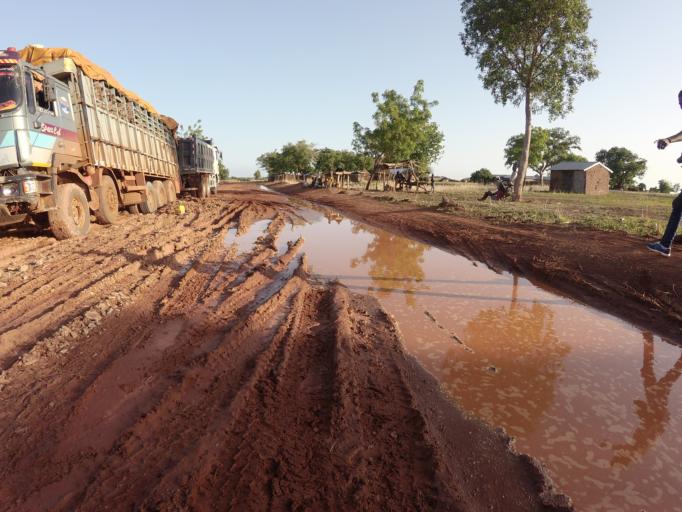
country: TG
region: Savanes
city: Sansanne-Mango
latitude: 10.3560
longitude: -0.0932
